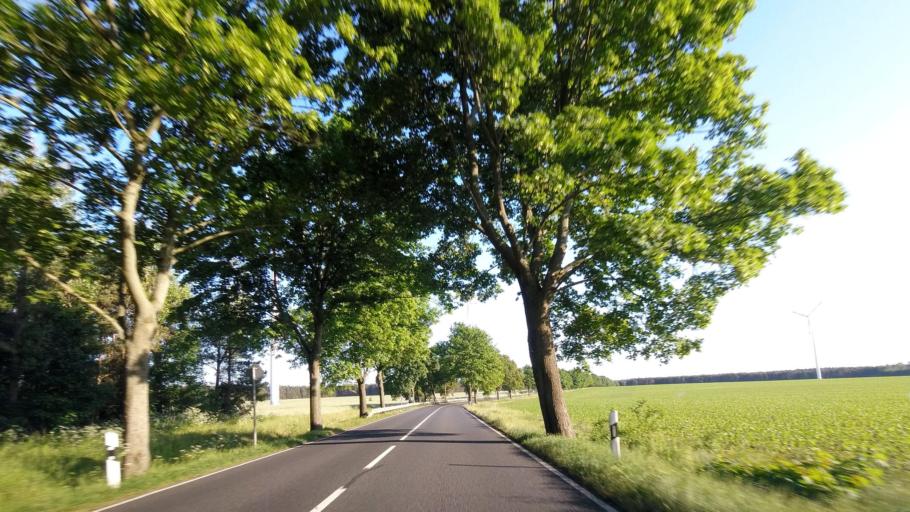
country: DE
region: Brandenburg
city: Golzow
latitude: 52.3124
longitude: 12.6091
